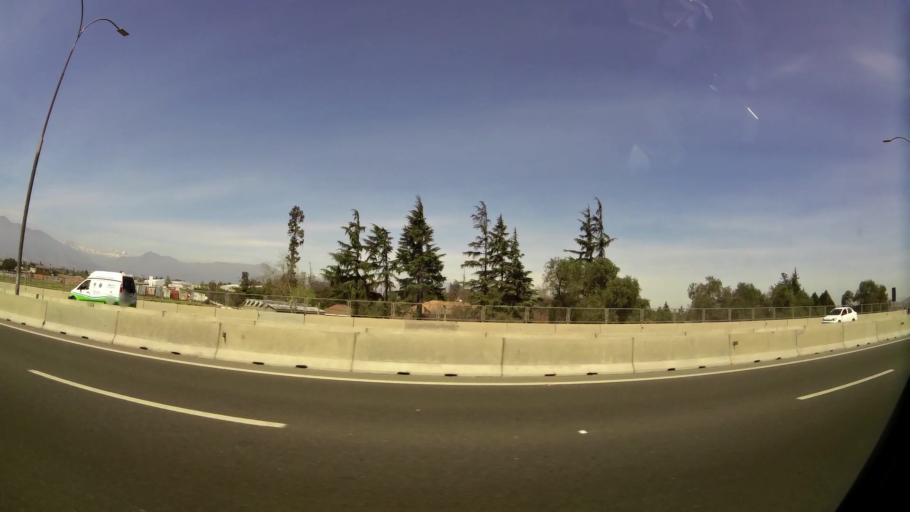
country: CL
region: Santiago Metropolitan
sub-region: Provincia de Maipo
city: San Bernardo
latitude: -33.5437
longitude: -70.6905
